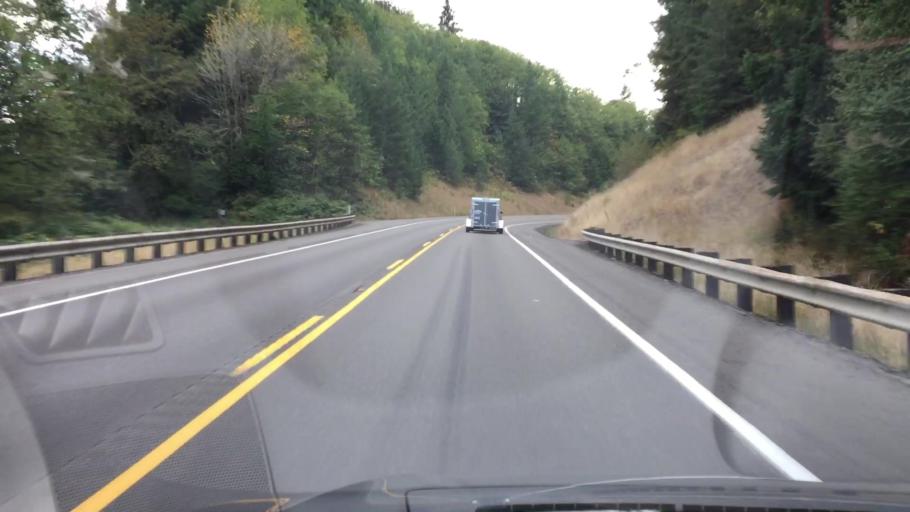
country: US
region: Washington
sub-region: Lewis County
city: Morton
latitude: 46.5137
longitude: -122.5740
